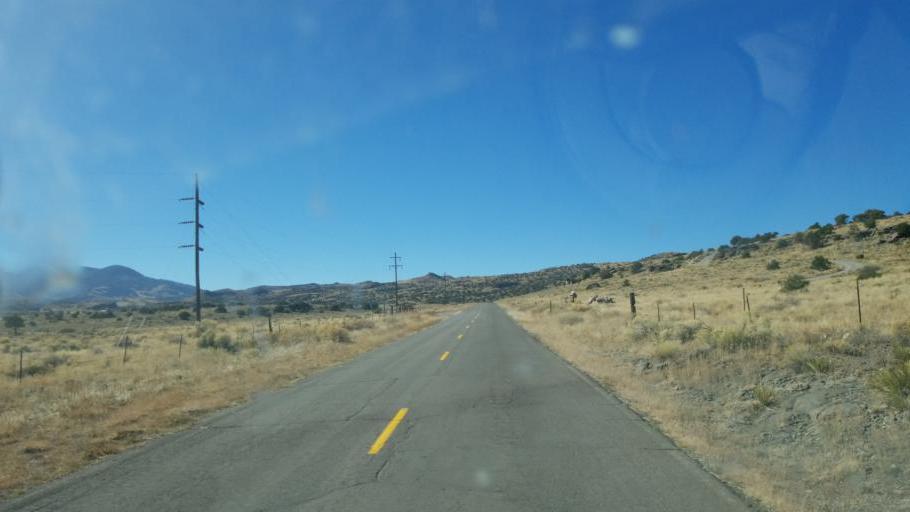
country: US
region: Colorado
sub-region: Rio Grande County
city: Del Norte
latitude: 37.6662
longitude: -106.3501
